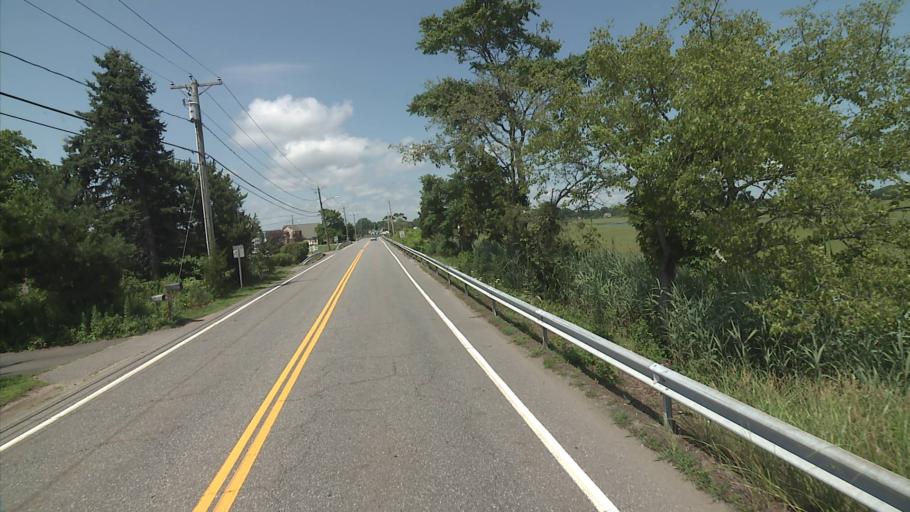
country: US
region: Connecticut
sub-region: Middlesex County
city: Saybrook Manor
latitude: 41.2747
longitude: -72.3934
